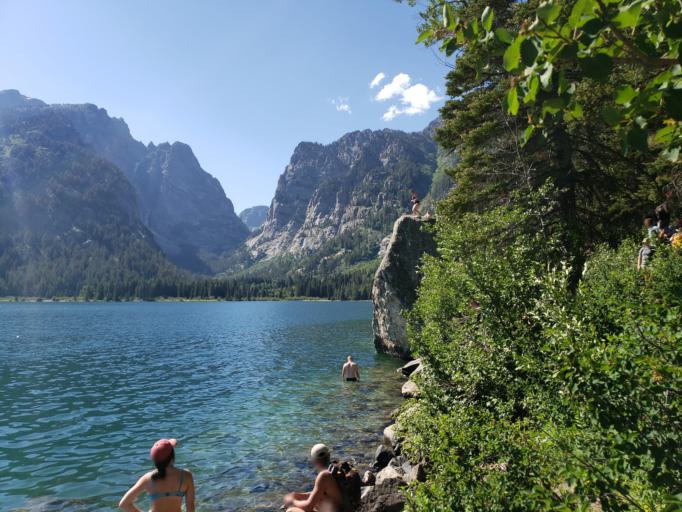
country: US
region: Wyoming
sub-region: Teton County
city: Moose Wilson Road
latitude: 43.6483
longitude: -110.7930
